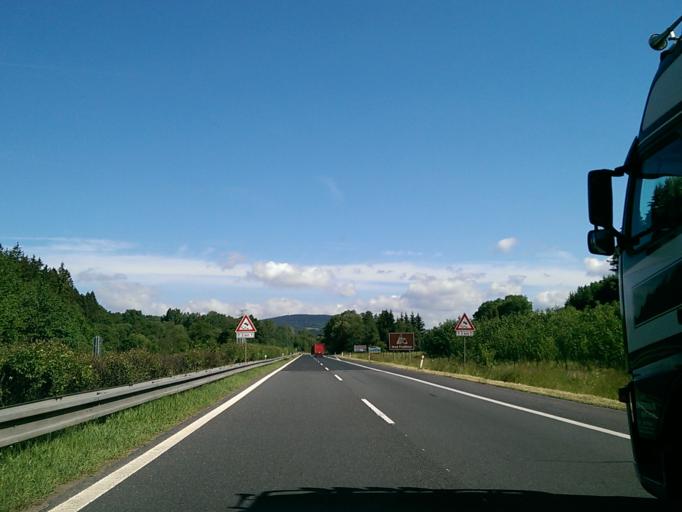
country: CZ
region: Liberecky
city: Hodkovice nad Mohelkou
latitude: 50.6441
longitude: 15.0984
